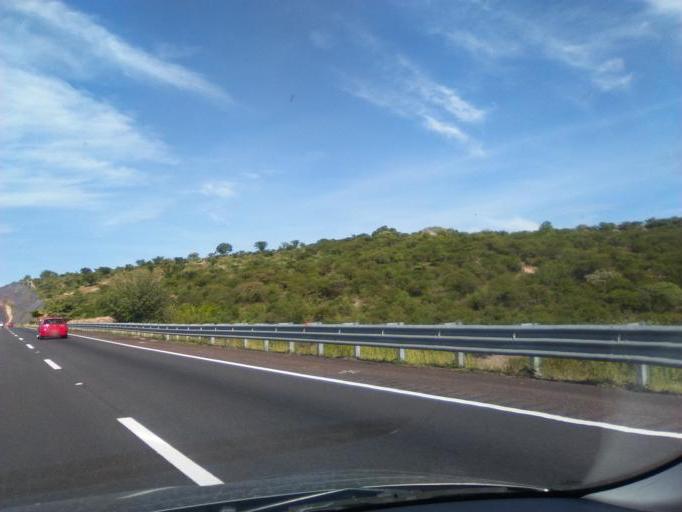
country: MX
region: Guerrero
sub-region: Huitzuco de los Figueroa
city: San Francisco Ozomatlan
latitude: 18.0223
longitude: -99.2721
